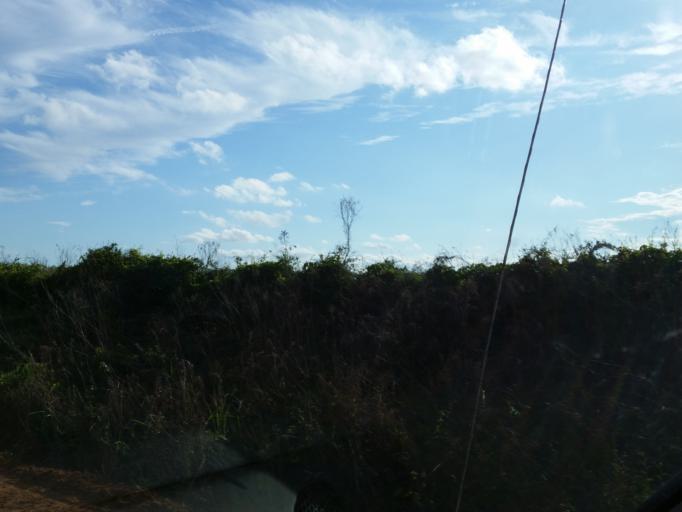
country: US
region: Georgia
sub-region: Crisp County
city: Cordele
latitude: 32.0176
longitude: -83.7736
